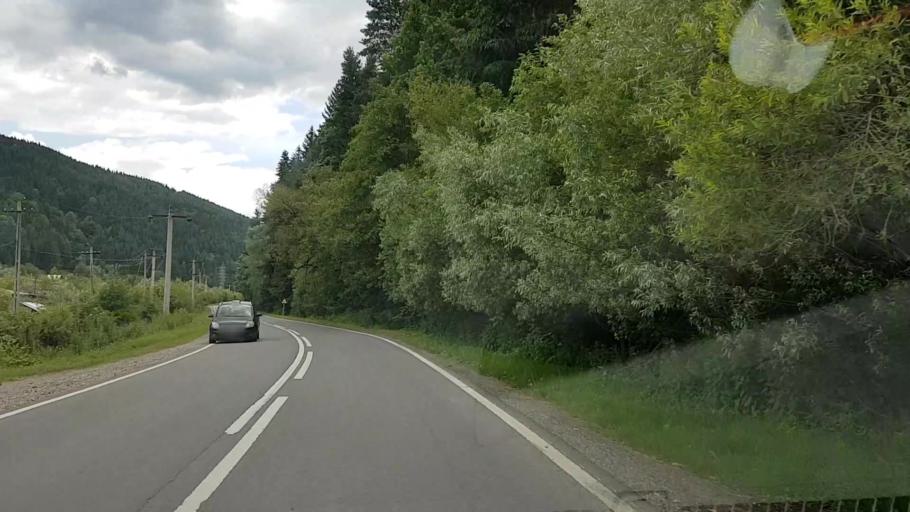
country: RO
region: Neamt
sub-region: Comuna Poiana Teiului
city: Poiana Teiului
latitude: 47.1050
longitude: 25.9359
